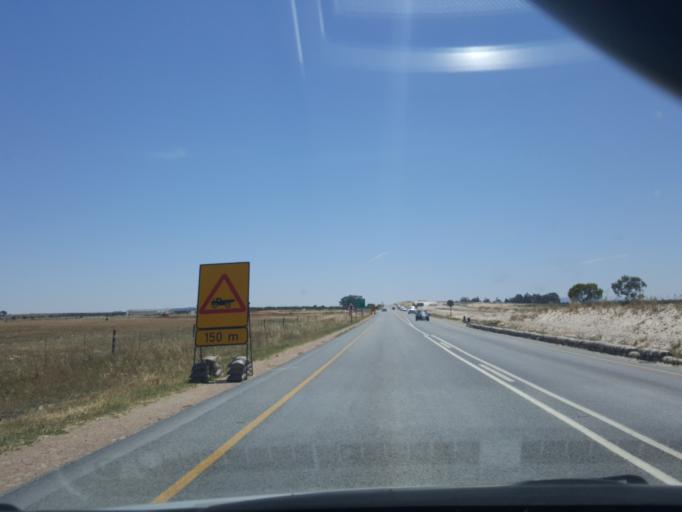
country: ZA
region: Western Cape
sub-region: City of Cape Town
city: Atlantis
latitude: -33.5719
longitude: 18.6187
